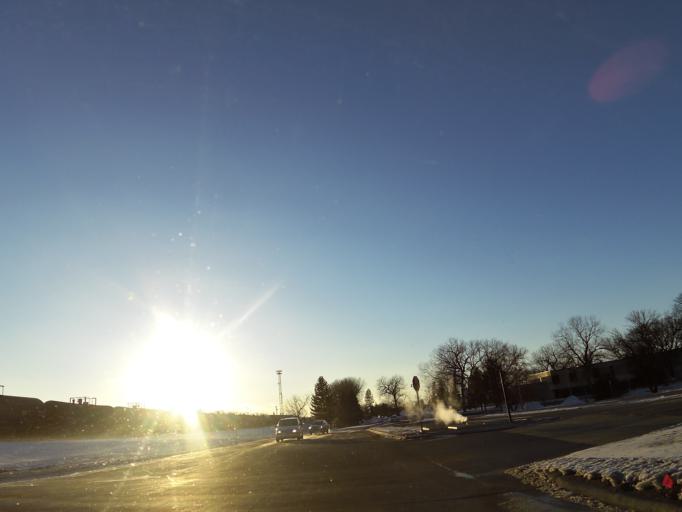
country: US
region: North Dakota
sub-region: Grand Forks County
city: Grand Forks
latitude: 47.9187
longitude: -97.0742
